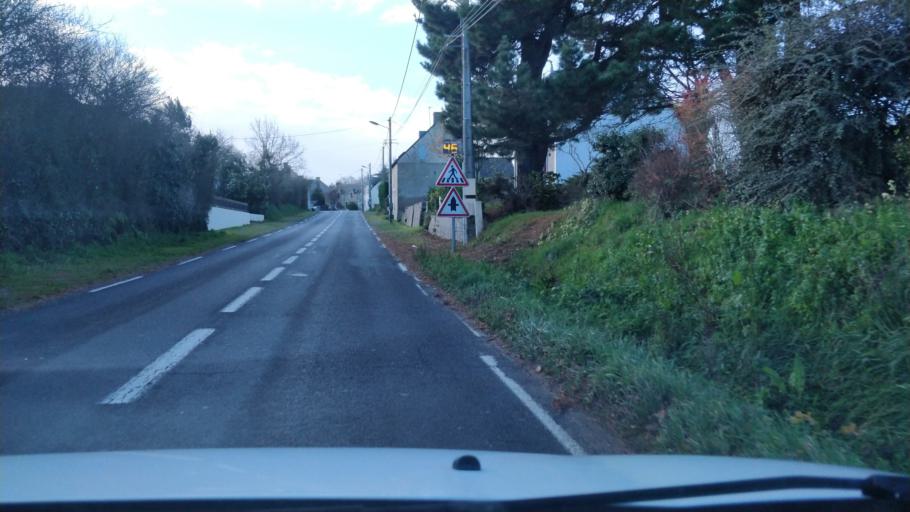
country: FR
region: Pays de la Loire
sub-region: Departement de la Loire-Atlantique
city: Asserac
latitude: 47.4173
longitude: -2.3999
